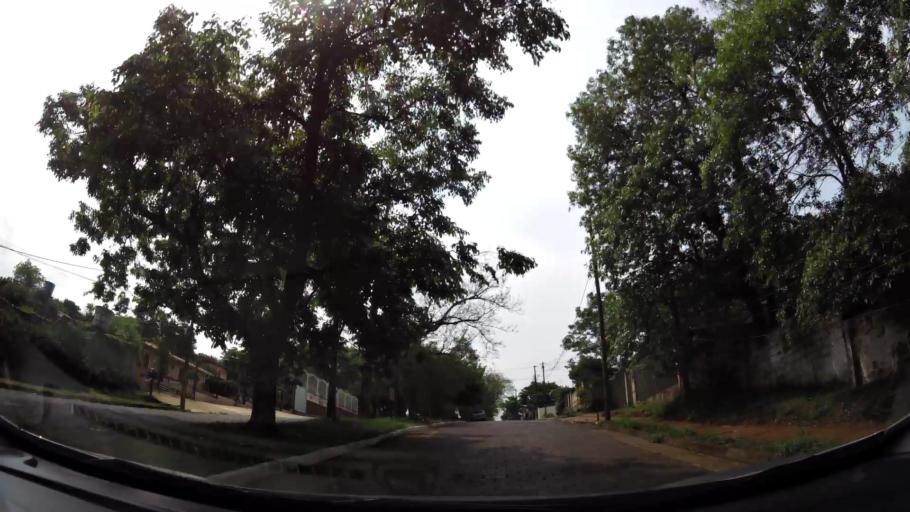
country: PY
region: Alto Parana
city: Presidente Franco
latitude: -25.5419
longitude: -54.6293
